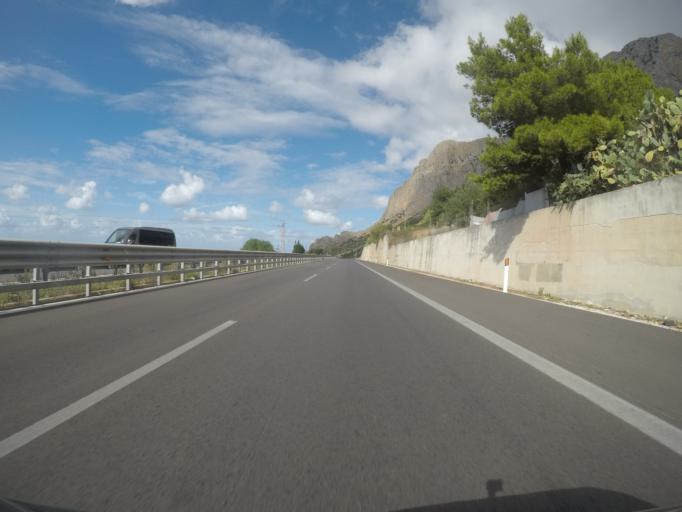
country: IT
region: Sicily
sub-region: Palermo
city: Cinisi
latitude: 38.1537
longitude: 13.1138
